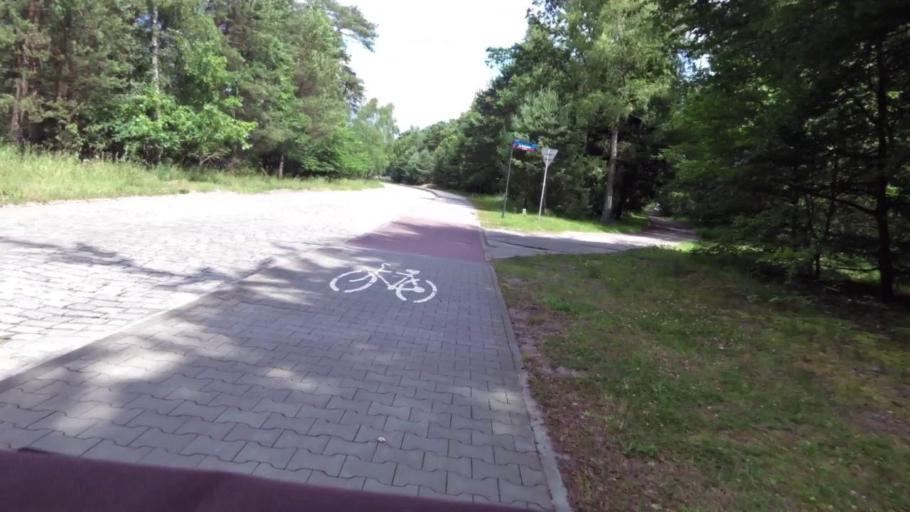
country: PL
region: West Pomeranian Voivodeship
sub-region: Powiat gryficki
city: Mrzezyno
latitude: 54.1362
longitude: 15.2733
